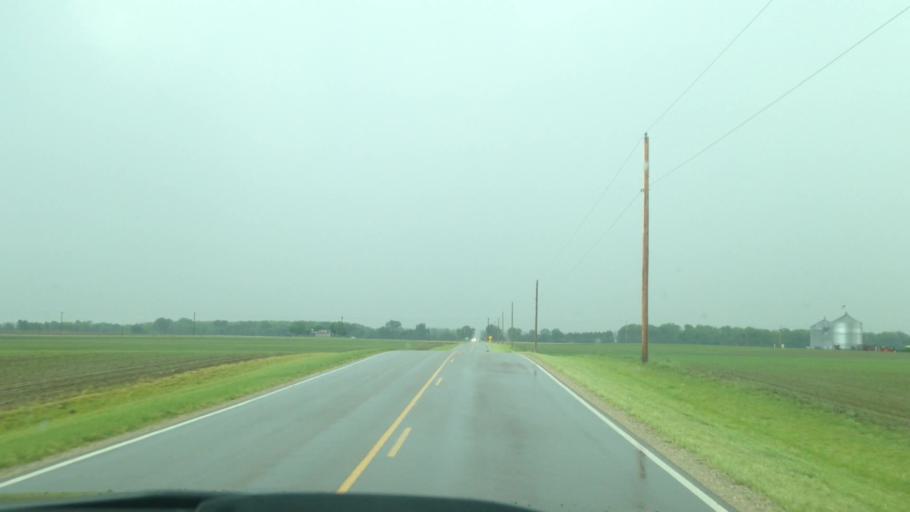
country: US
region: Ohio
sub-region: Darke County
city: Greenville
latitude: 40.1504
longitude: -84.6431
